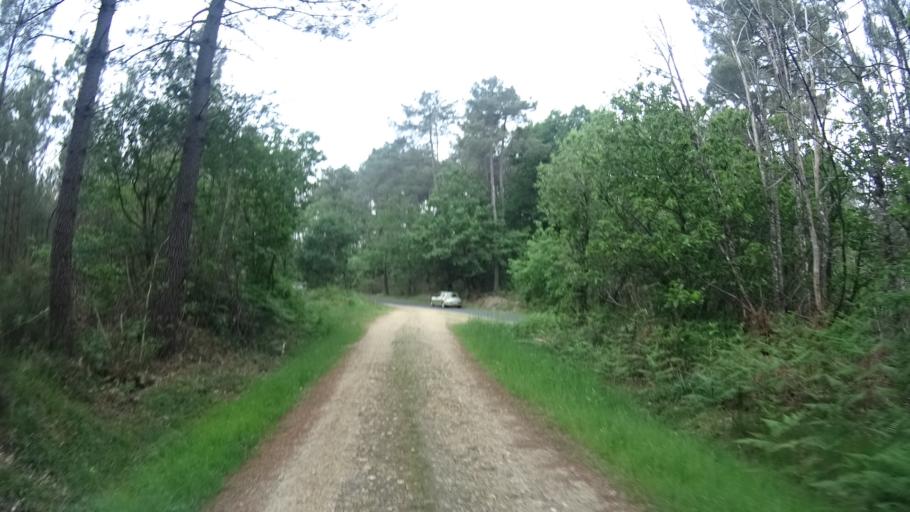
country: FR
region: Aquitaine
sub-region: Departement de la Dordogne
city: Neuvic
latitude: 45.0379
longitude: 0.4611
